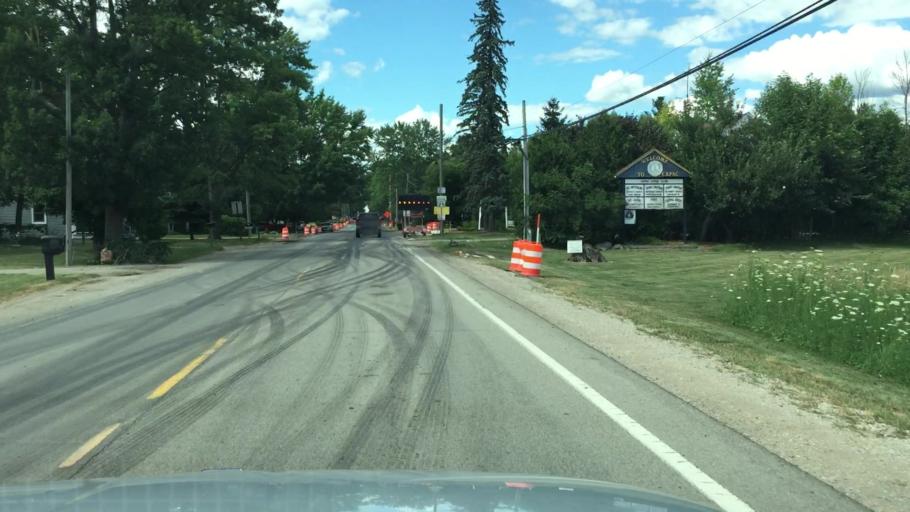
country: US
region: Michigan
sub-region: Saint Clair County
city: Capac
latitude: 43.0047
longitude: -82.9283
